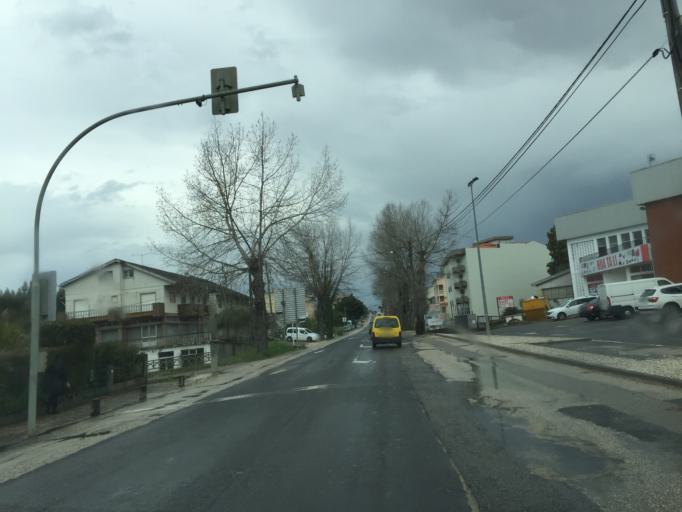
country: PT
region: Santarem
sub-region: Ourem
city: Fatima
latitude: 39.6360
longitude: -8.6841
